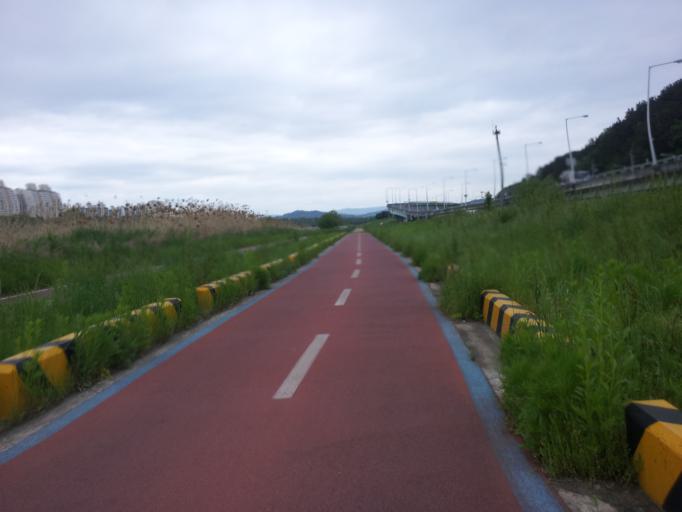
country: KR
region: Daejeon
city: Daejeon
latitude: 36.3601
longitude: 127.4028
